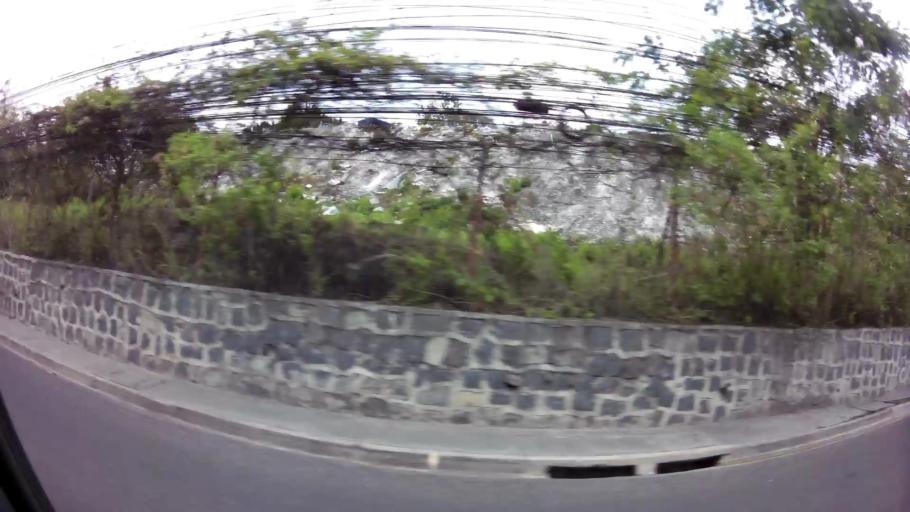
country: HN
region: Francisco Morazan
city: Tegucigalpa
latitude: 14.0589
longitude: -87.2317
